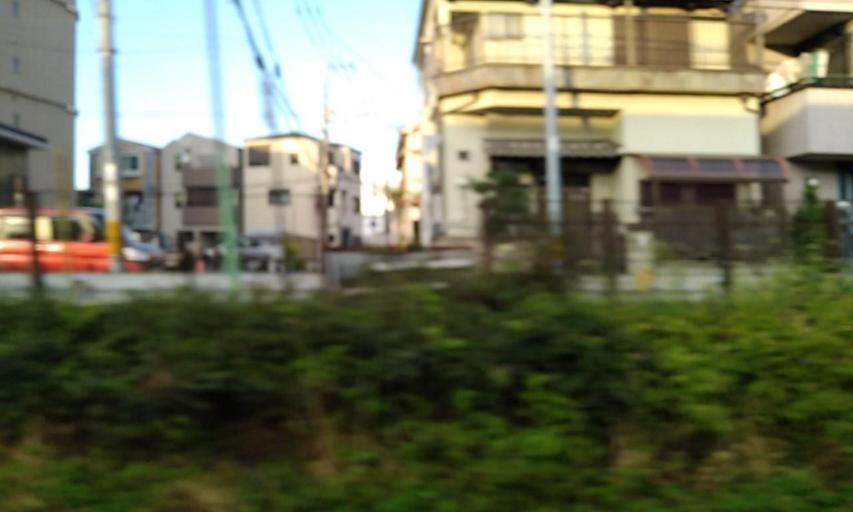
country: JP
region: Osaka
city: Sakai
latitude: 34.5669
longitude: 135.4906
